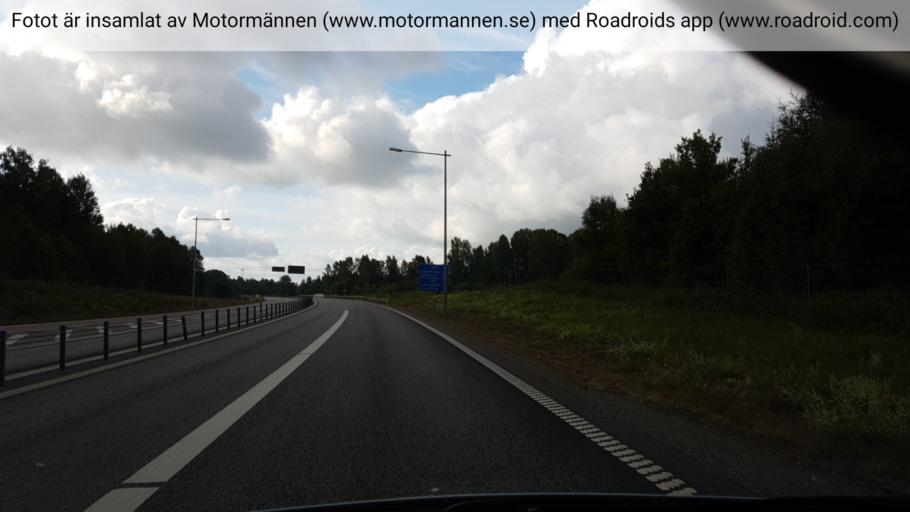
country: SE
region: Vaestra Goetaland
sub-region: Skovde Kommun
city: Skoevde
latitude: 58.3659
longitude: 13.8566
